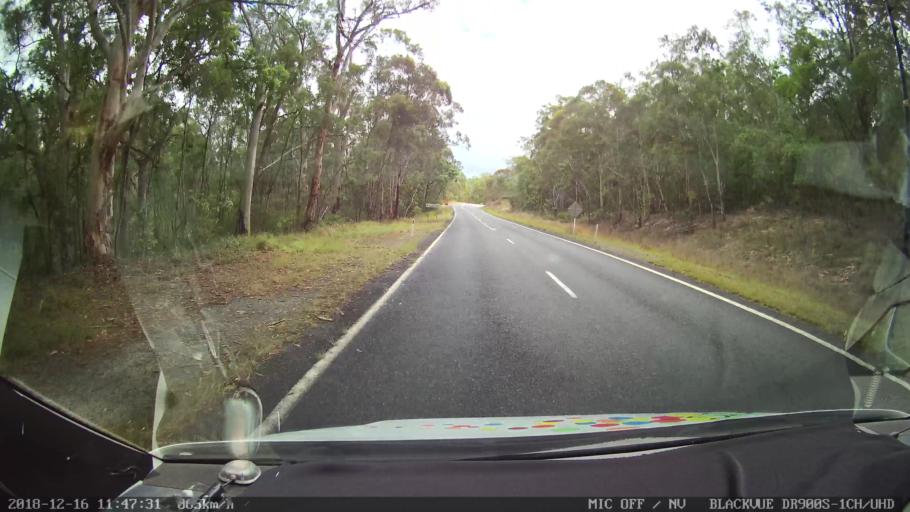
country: AU
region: New South Wales
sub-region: Tenterfield Municipality
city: Carrolls Creek
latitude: -28.9211
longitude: 152.2389
